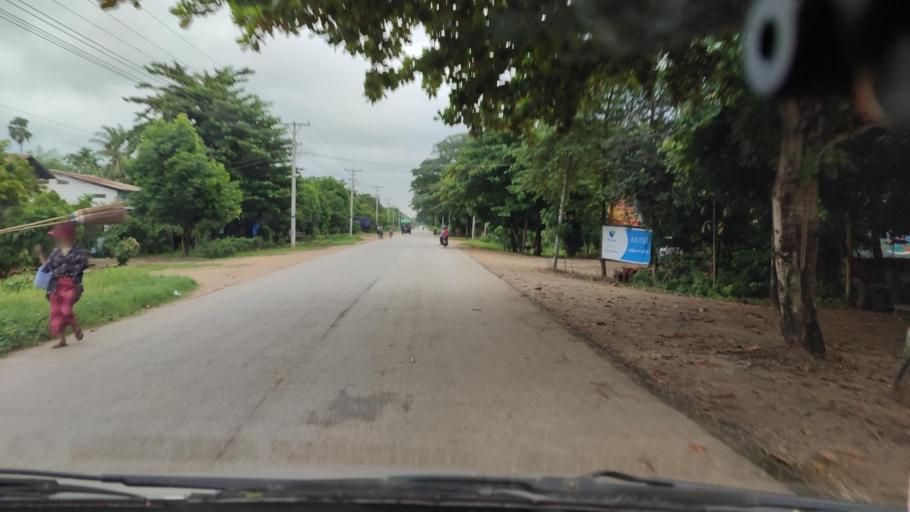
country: MM
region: Bago
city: Pyay
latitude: 18.8538
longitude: 95.3943
